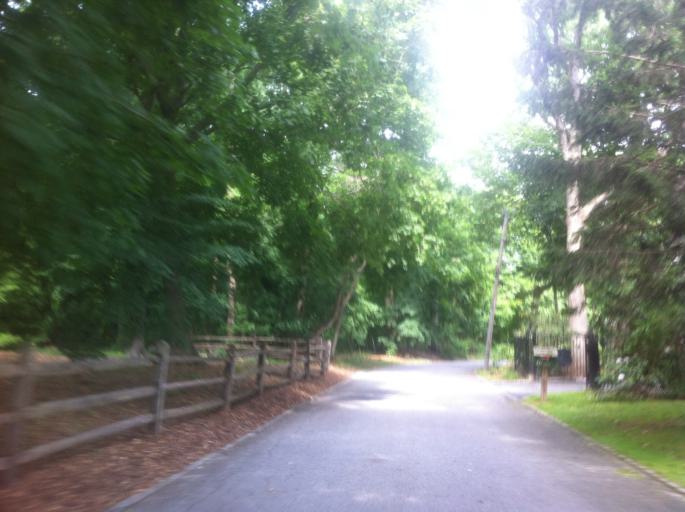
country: US
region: New York
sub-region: Nassau County
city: Locust Valley
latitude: 40.8624
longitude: -73.5795
